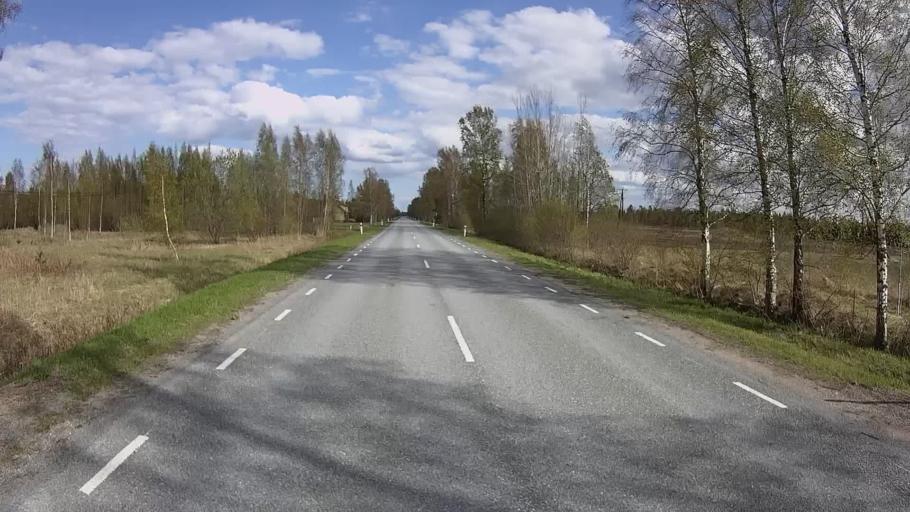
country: EE
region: Jogevamaa
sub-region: Mustvee linn
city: Mustvee
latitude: 58.7911
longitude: 26.9512
